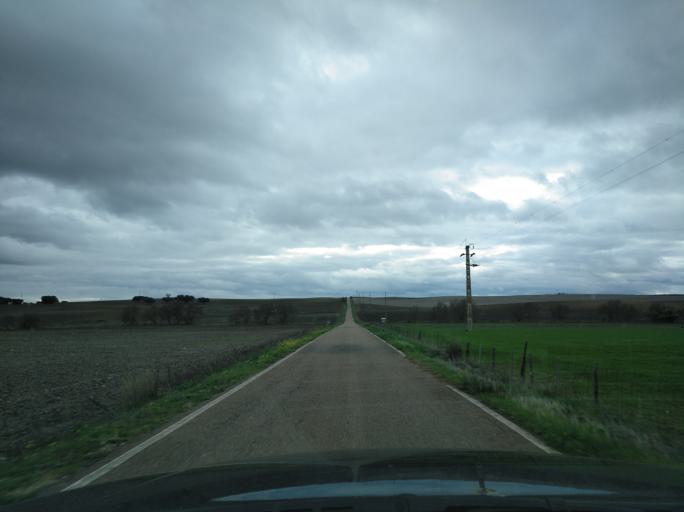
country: PT
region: Portalegre
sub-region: Campo Maior
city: Campo Maior
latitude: 38.9843
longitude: -7.0079
